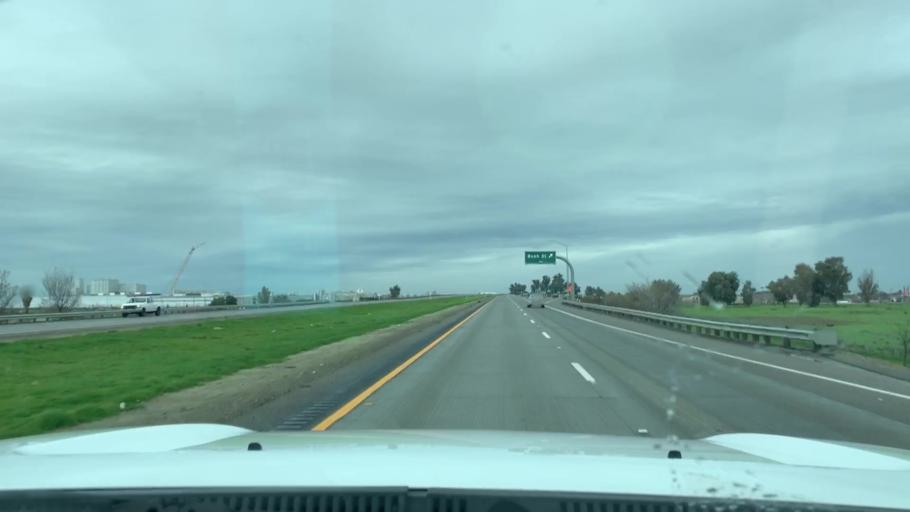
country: US
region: California
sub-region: Kings County
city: Lemoore
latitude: 36.2923
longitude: -119.8090
